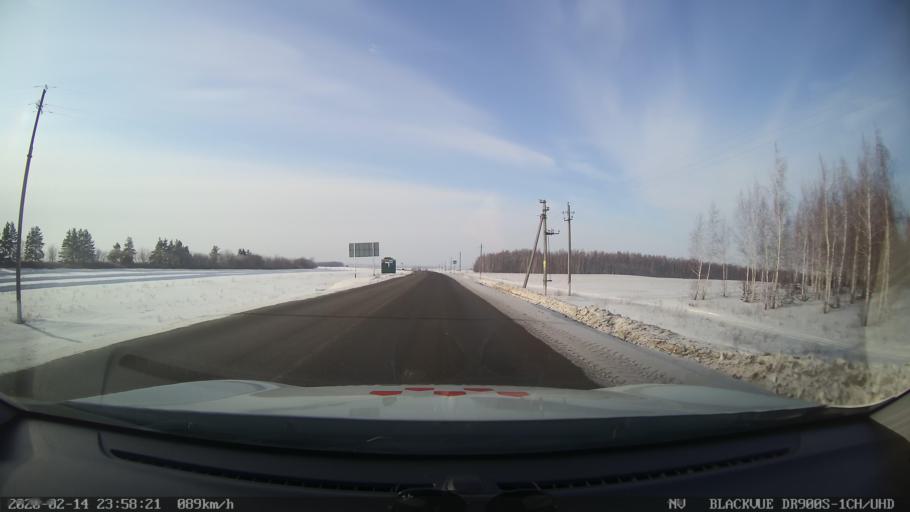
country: RU
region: Tatarstan
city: Kuybyshevskiy Zaton
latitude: 55.3403
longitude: 49.0891
